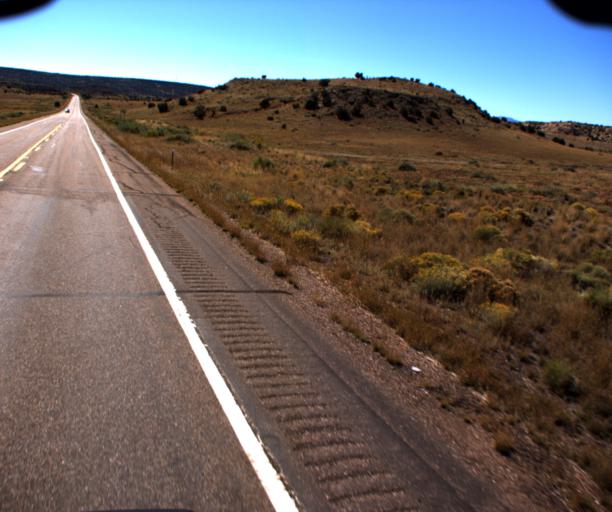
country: US
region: Arizona
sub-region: Apache County
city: Saint Johns
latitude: 34.3999
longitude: -109.4101
